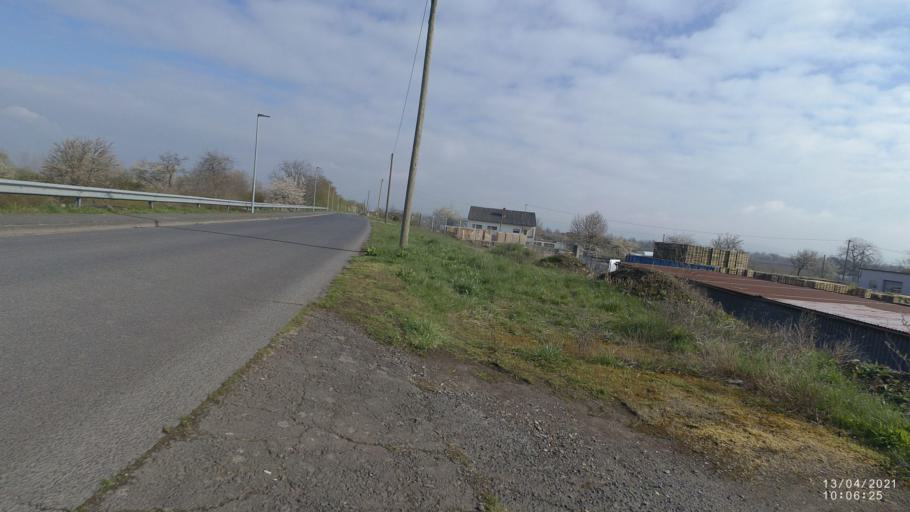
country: DE
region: Rheinland-Pfalz
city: Urmitz
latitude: 50.4040
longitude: 7.5105
